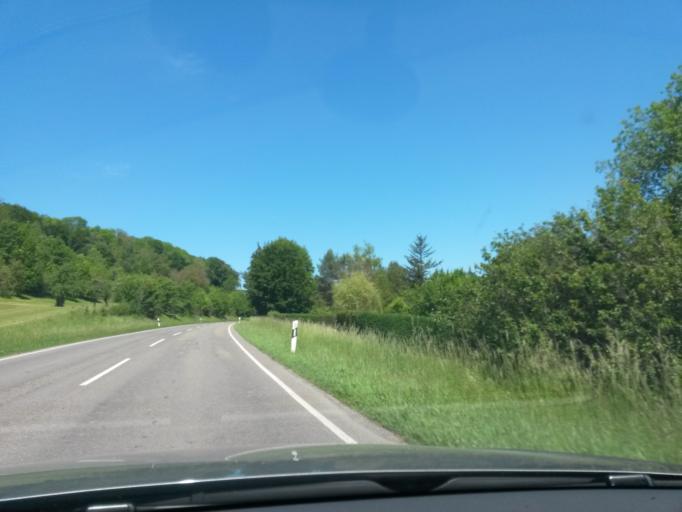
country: DE
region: Baden-Wuerttemberg
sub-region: Regierungsbezirk Stuttgart
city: Weil der Stadt
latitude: 48.7403
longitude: 8.8727
